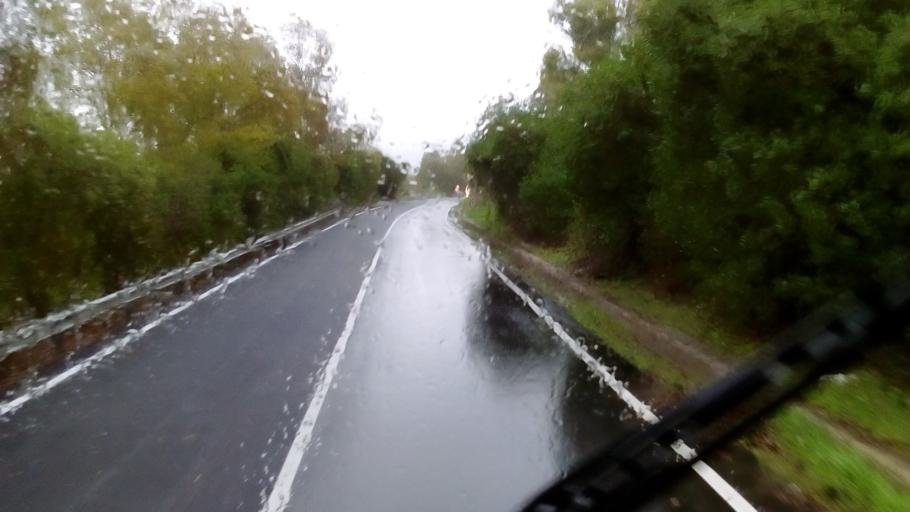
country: IT
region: Sicily
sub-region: Enna
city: Pietraperzia
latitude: 37.4729
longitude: 14.1665
